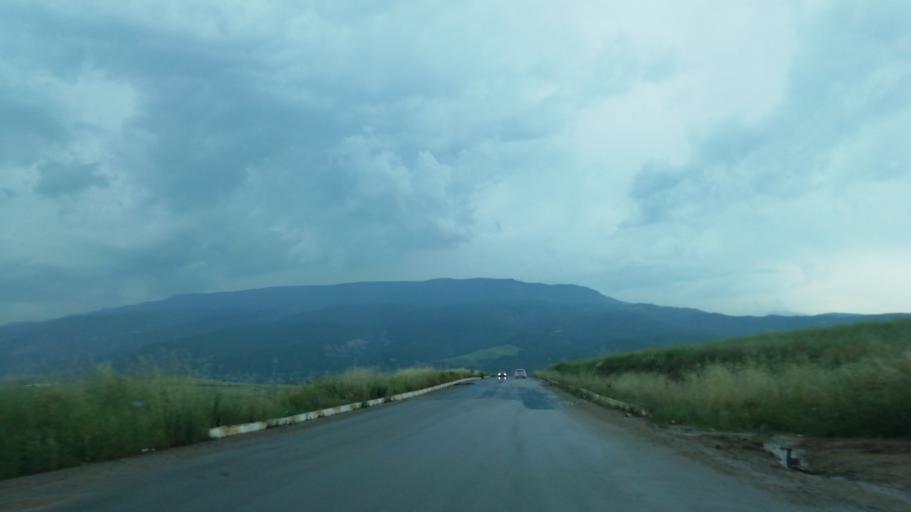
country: TR
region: Karabuk
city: Safranbolu
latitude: 41.2342
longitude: 32.6840
